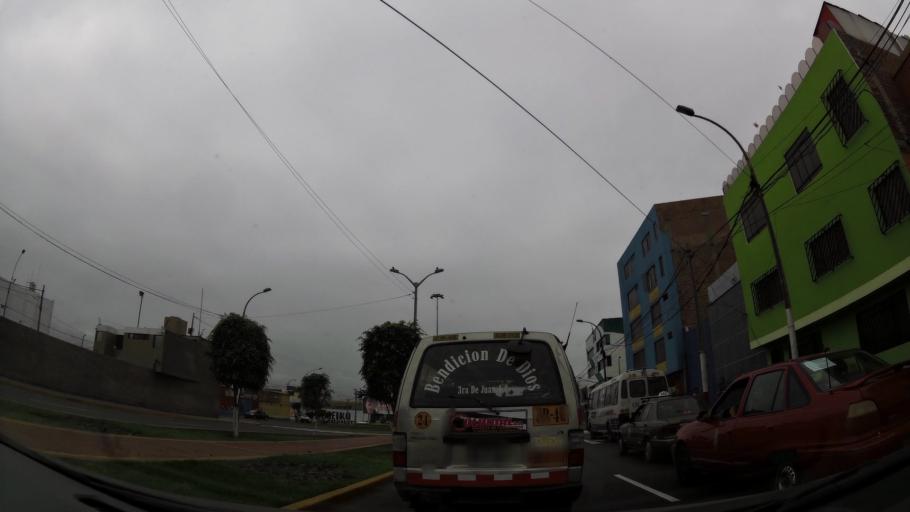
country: PE
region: Callao
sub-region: Callao
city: Callao
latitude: -12.0610
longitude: -77.1330
